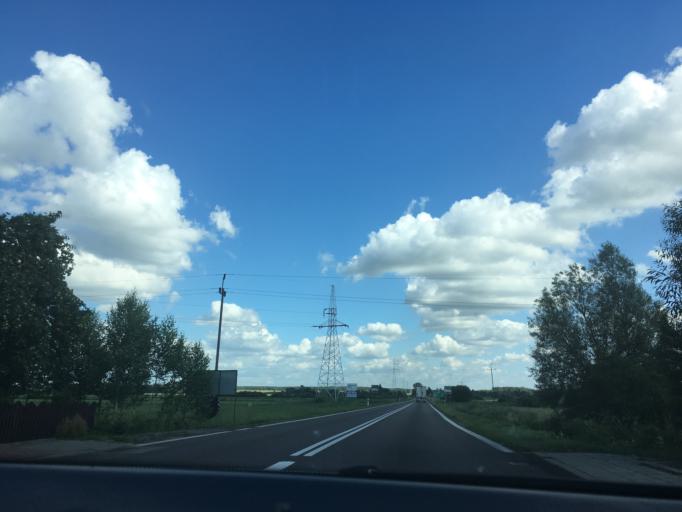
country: PL
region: Podlasie
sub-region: Powiat sokolski
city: Suchowola
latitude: 53.6769
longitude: 23.1052
